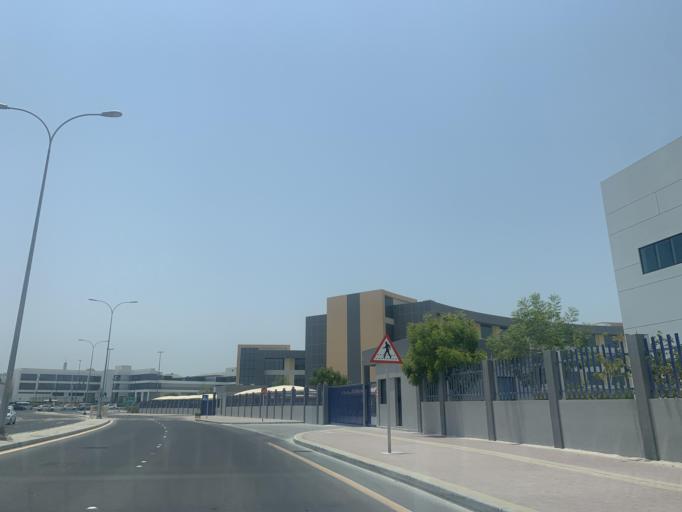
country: BH
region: Muharraq
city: Al Muharraq
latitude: 26.3052
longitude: 50.6355
